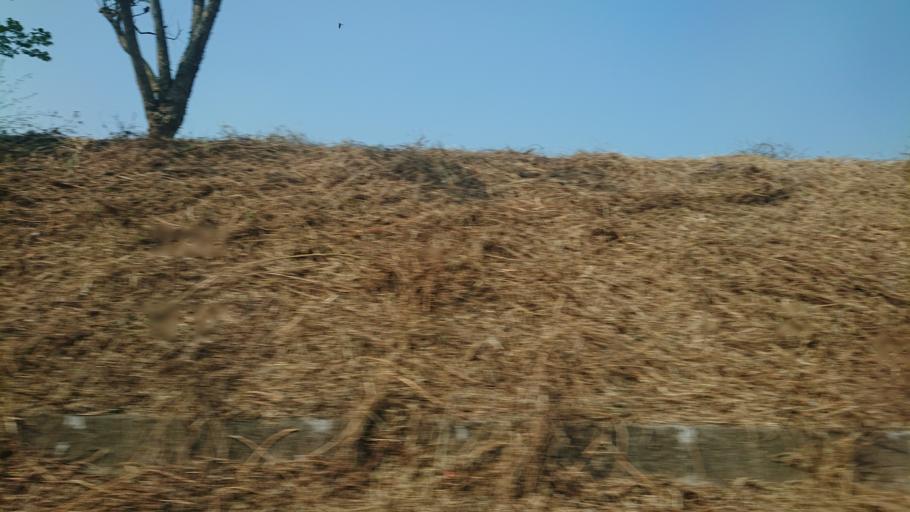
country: TW
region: Taiwan
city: Lugu
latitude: 23.7462
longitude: 120.6585
